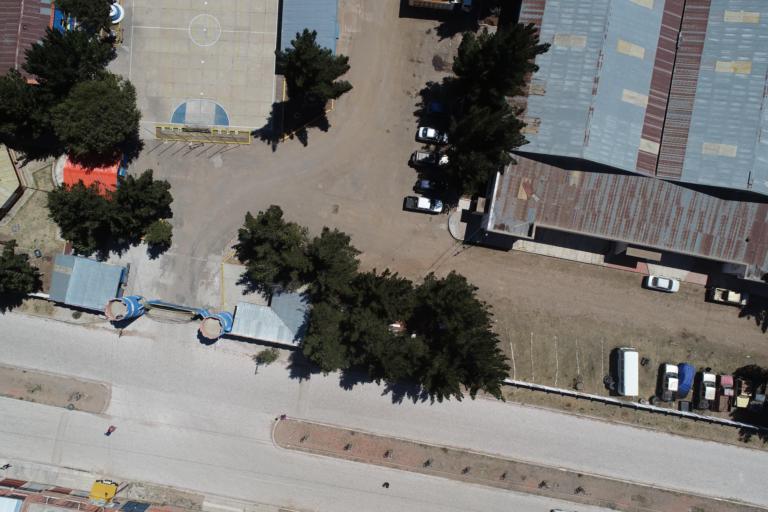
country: BO
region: La Paz
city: La Paz
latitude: -16.5687
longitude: -68.1905
